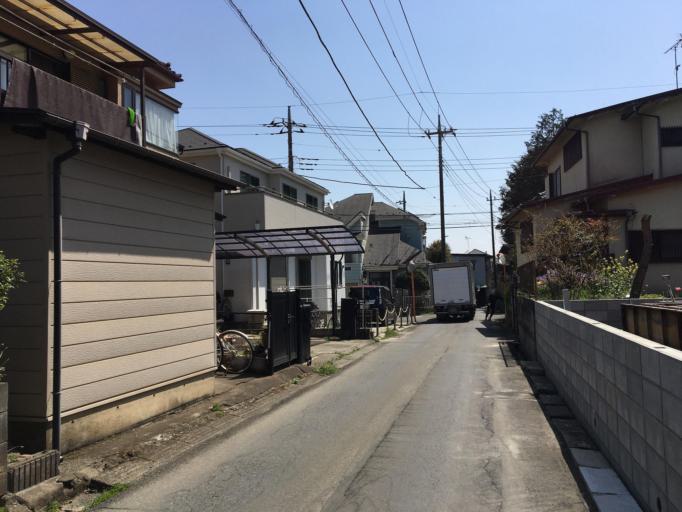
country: JP
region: Saitama
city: Sayama
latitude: 35.8925
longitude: 139.3711
